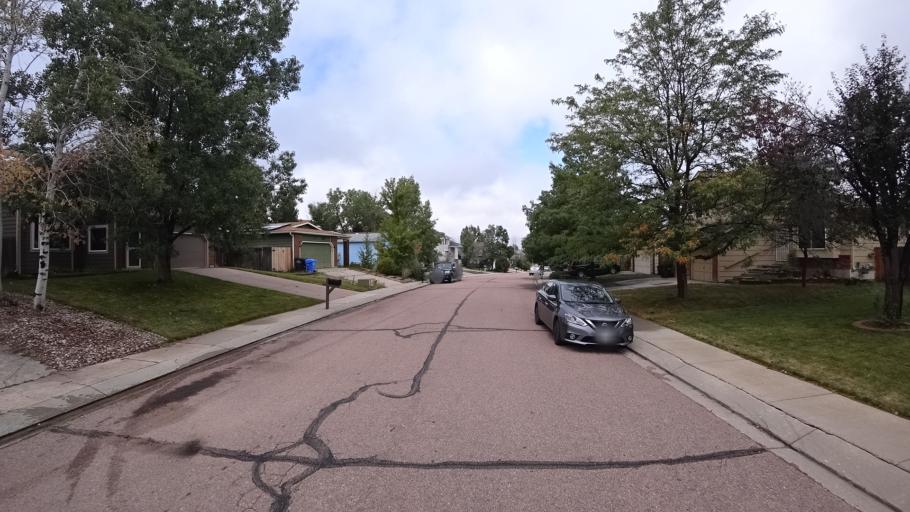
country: US
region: Colorado
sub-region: El Paso County
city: Cimarron Hills
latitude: 38.9217
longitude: -104.7641
